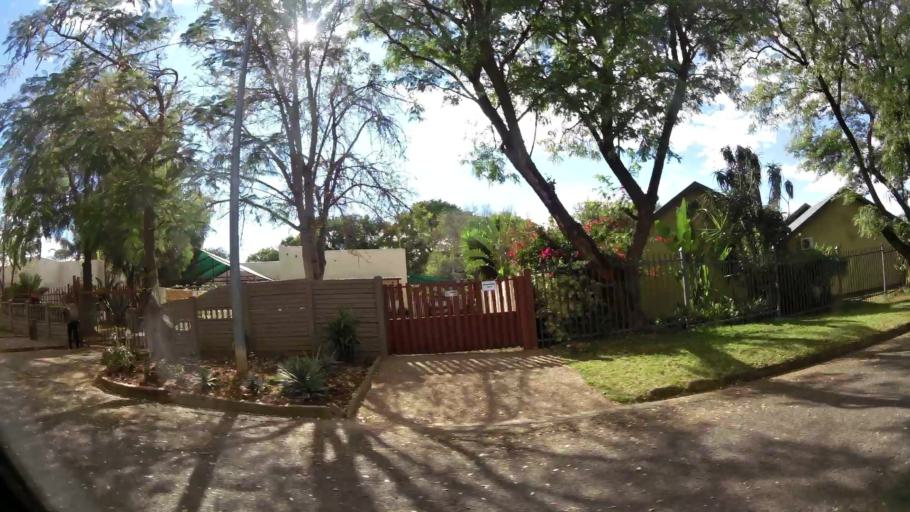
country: ZA
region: Limpopo
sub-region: Waterberg District Municipality
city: Warmbaths
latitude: -24.8769
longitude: 28.2815
